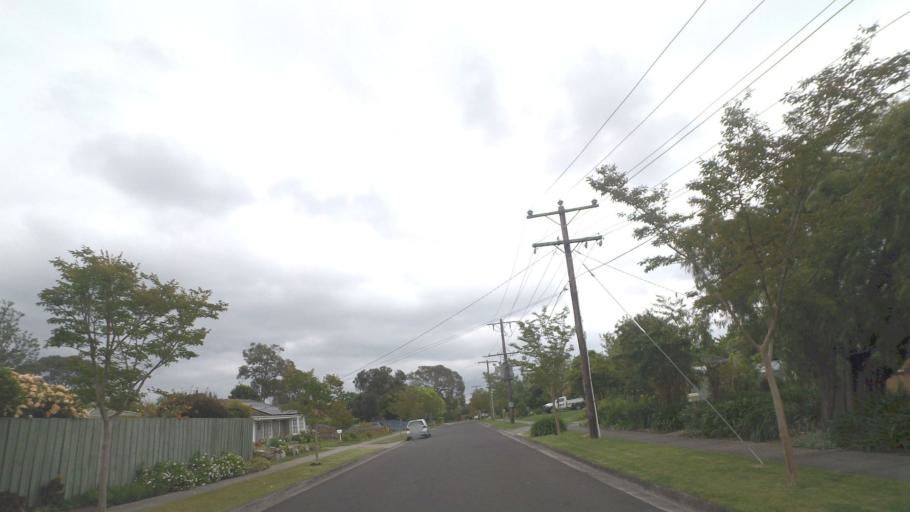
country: AU
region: Victoria
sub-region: Knox
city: Bayswater
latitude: -37.8524
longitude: 145.2723
